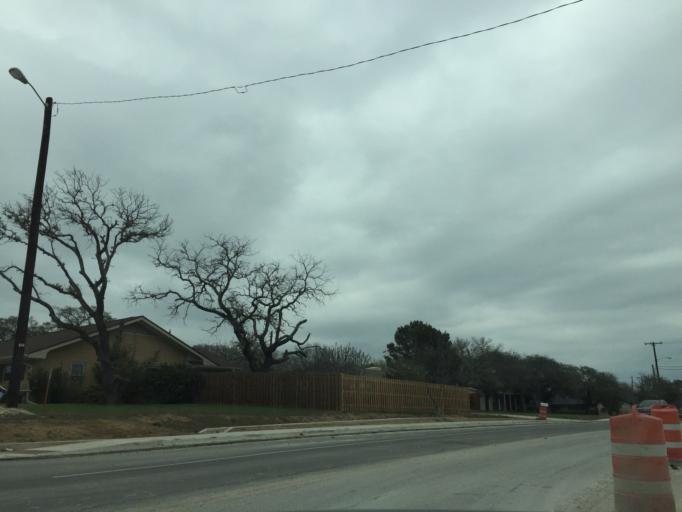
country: US
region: Texas
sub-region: Bell County
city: Harker Heights
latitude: 31.0733
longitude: -97.6725
